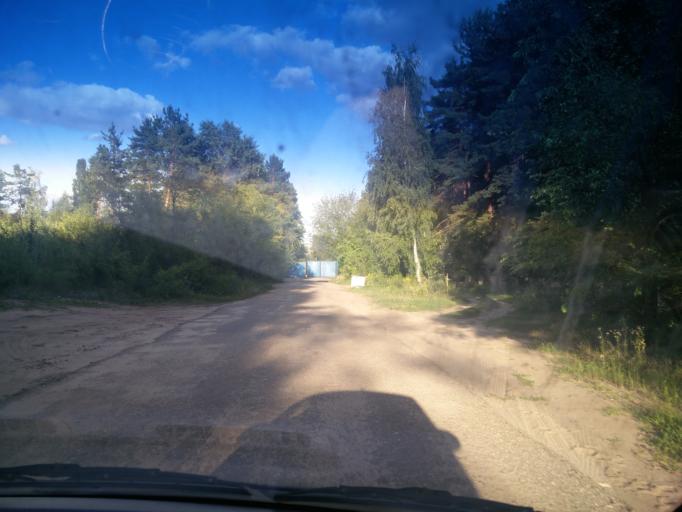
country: RU
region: Voronezj
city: Pridonskoy
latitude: 51.6738
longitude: 39.1140
